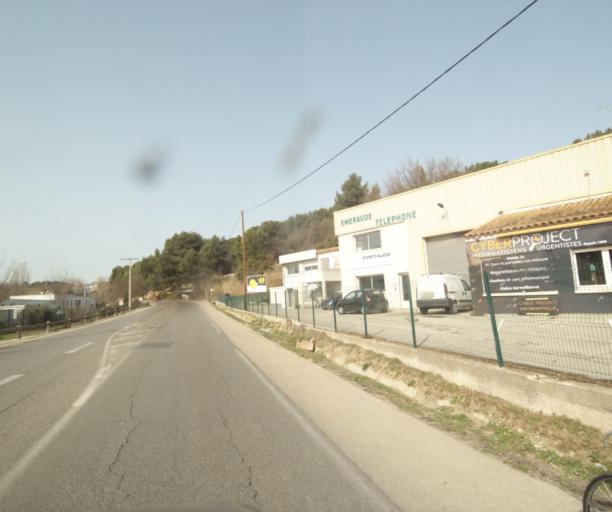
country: FR
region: Provence-Alpes-Cote d'Azur
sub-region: Departement des Bouches-du-Rhone
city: Aix-en-Provence
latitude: 43.5107
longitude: 5.4142
